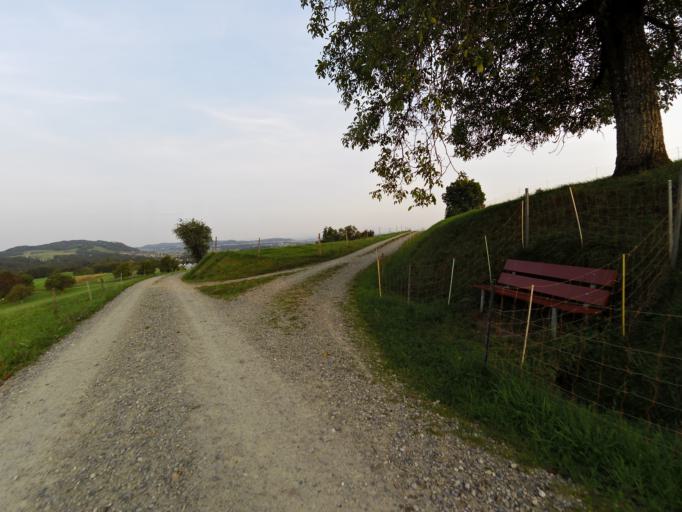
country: CH
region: Thurgau
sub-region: Frauenfeld District
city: Frauenfeld
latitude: 47.5303
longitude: 8.8970
